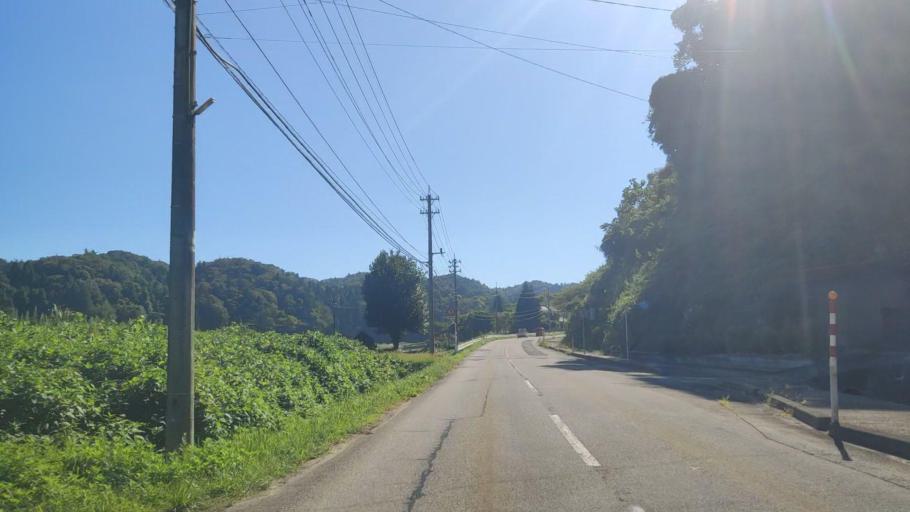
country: JP
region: Ishikawa
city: Nanao
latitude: 37.3392
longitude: 137.2172
